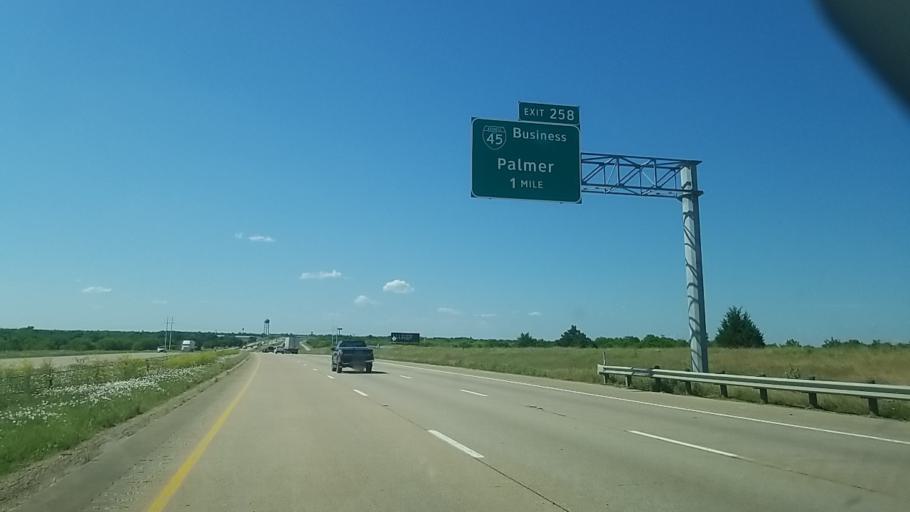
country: US
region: Texas
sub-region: Ellis County
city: Palmer
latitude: 32.3996
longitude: -96.6547
